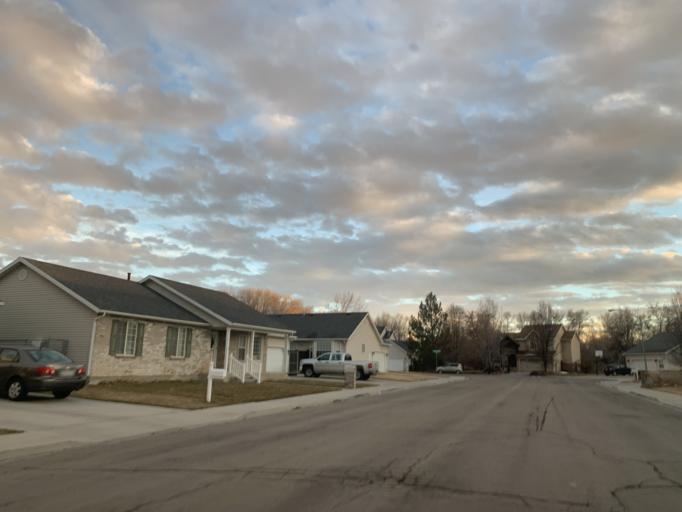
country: US
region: Utah
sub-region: Utah County
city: Provo
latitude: 40.2395
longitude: -111.6994
